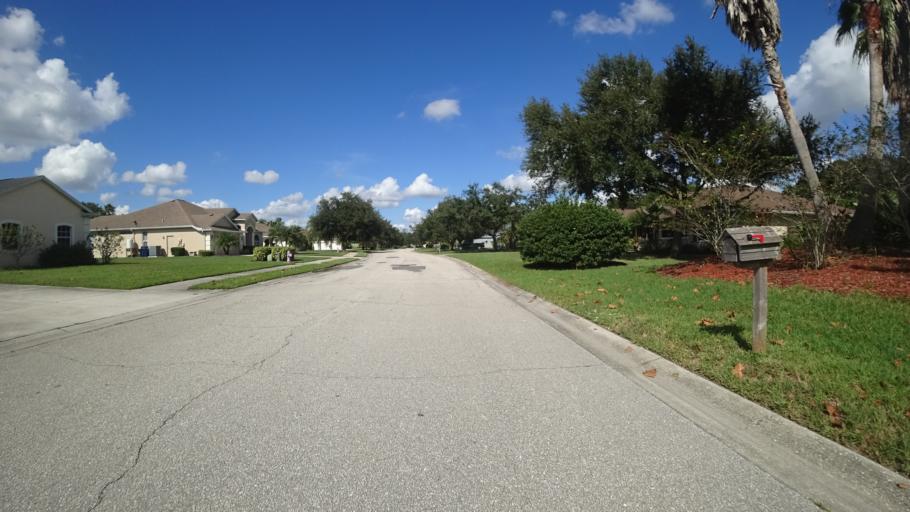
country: US
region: Florida
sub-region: Manatee County
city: Ellenton
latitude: 27.4986
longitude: -82.3974
